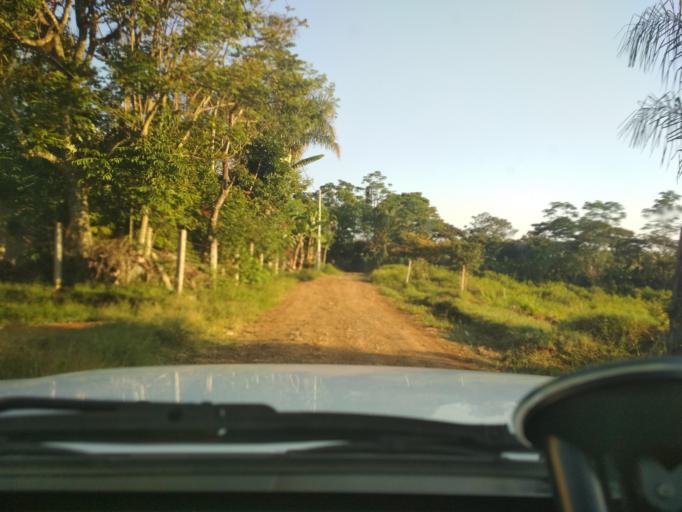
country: MX
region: Veracruz
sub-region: Fortin
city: Fraccionamiento Villas de la Llave
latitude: 18.9214
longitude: -96.9999
